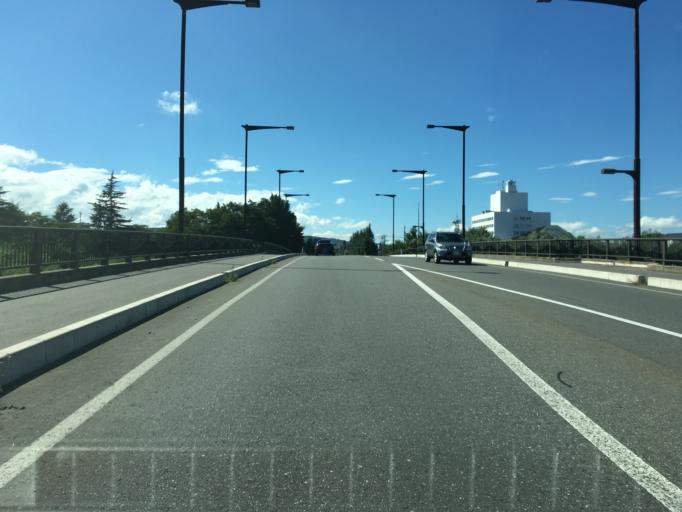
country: JP
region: Yamagata
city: Yonezawa
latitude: 37.9207
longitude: 140.1201
